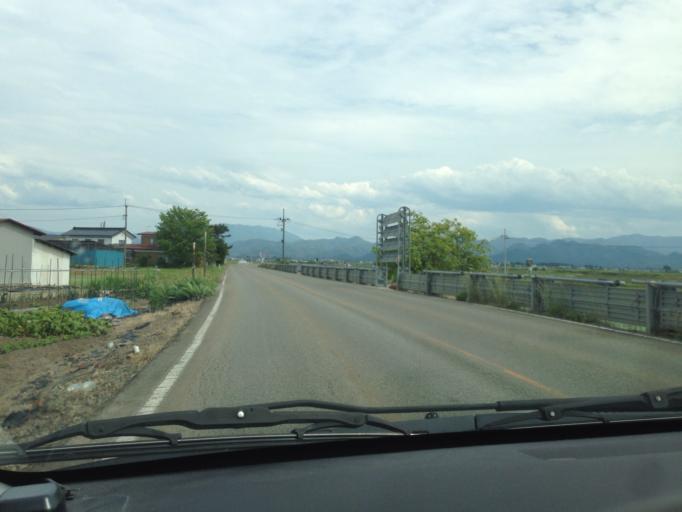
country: JP
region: Fukushima
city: Kitakata
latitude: 37.4860
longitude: 139.8381
